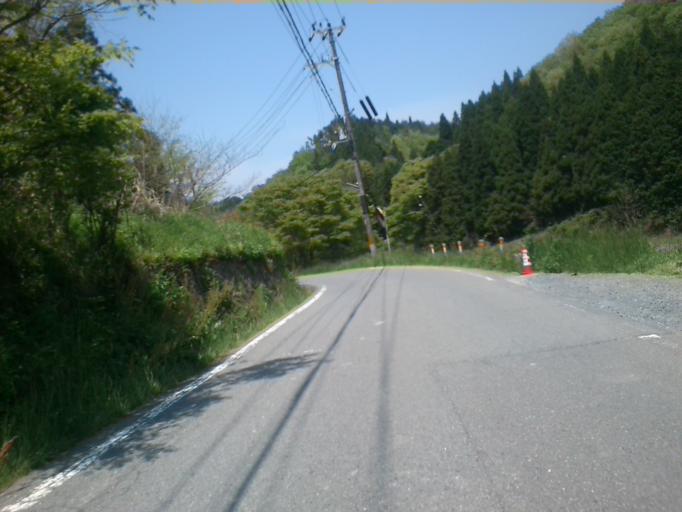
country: JP
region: Kyoto
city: Kameoka
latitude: 34.9412
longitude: 135.5352
